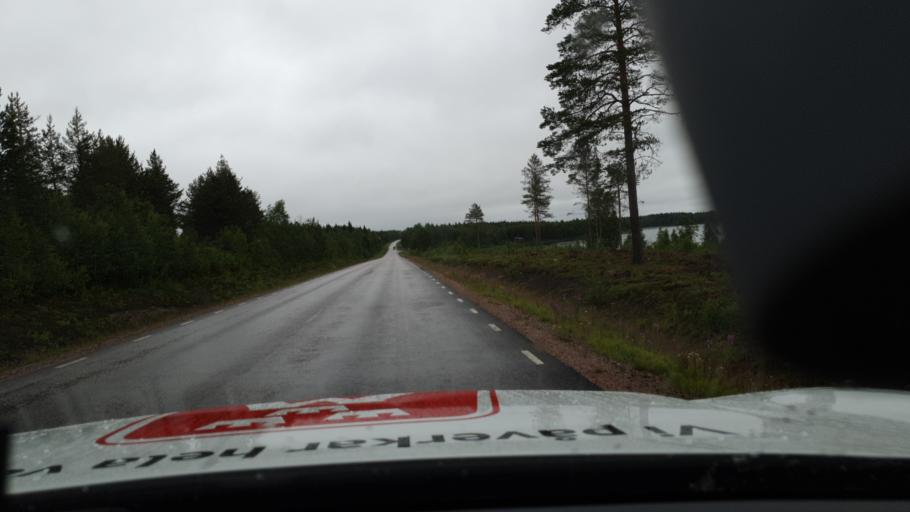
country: SE
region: Norrbotten
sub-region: Overtornea Kommun
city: OEvertornea
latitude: 66.4898
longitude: 23.7084
